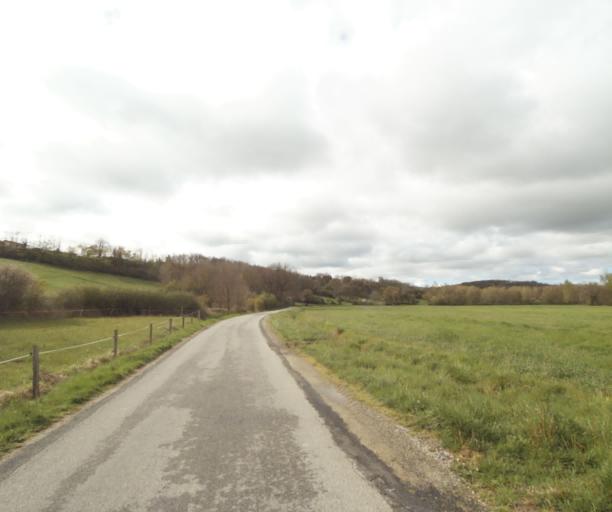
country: FR
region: Midi-Pyrenees
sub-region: Departement de l'Ariege
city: Saverdun
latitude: 43.2314
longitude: 1.5636
